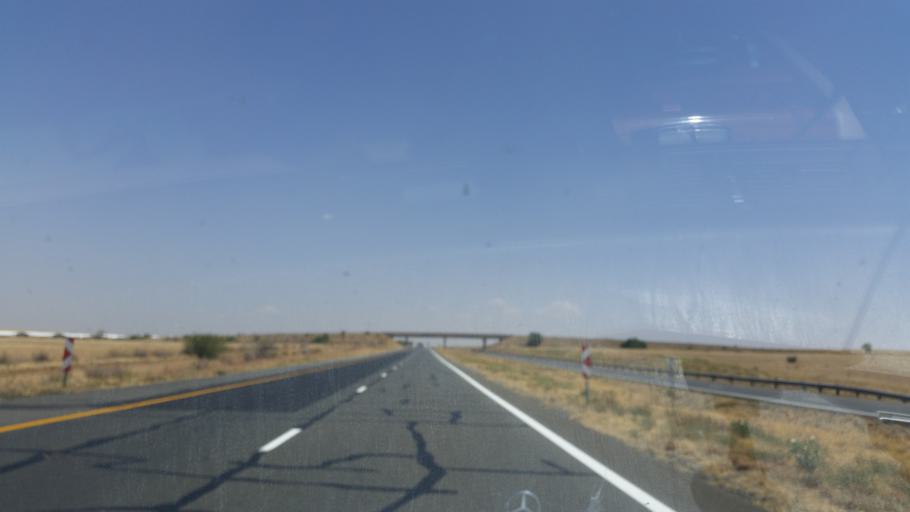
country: ZA
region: Orange Free State
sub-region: Lejweleputswa District Municipality
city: Brandfort
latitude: -28.8652
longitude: 26.5352
